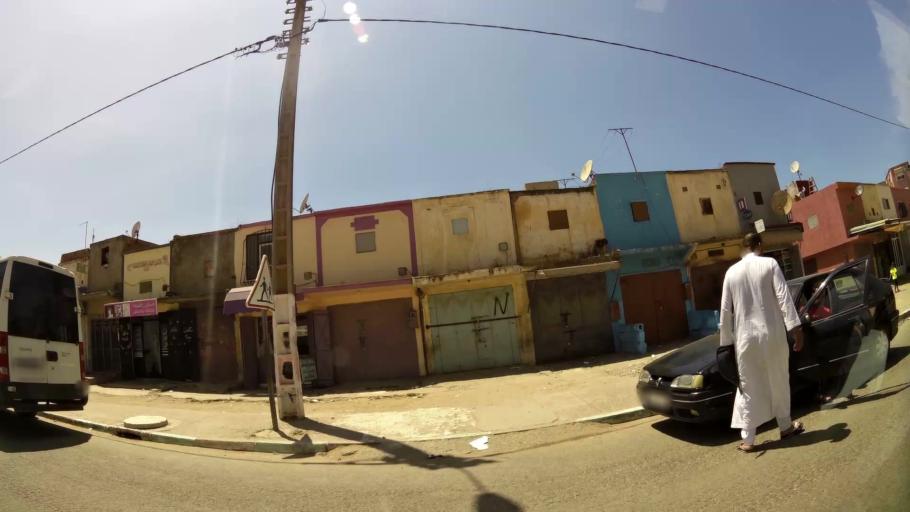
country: MA
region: Gharb-Chrarda-Beni Hssen
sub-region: Kenitra Province
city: Kenitra
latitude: 34.2542
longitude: -6.5457
